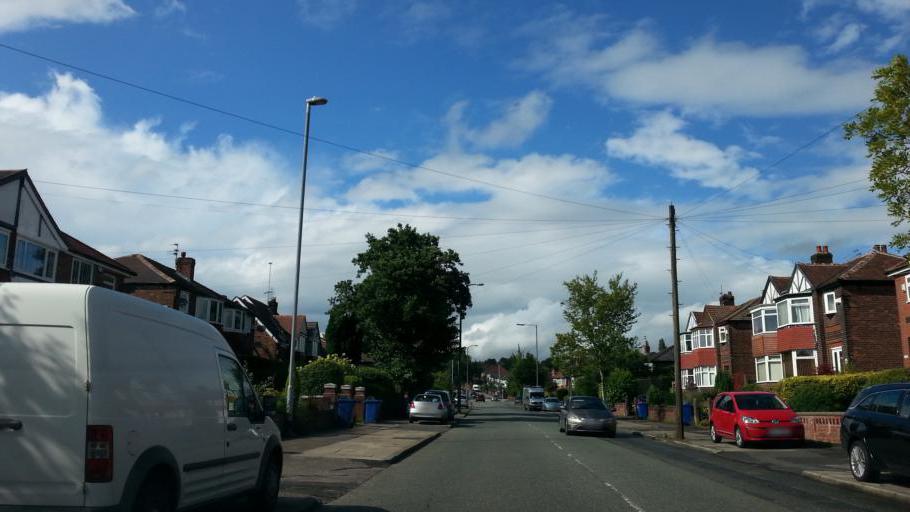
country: GB
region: England
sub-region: Borough of Bury
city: Prestwich
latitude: 53.5326
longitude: -2.2742
